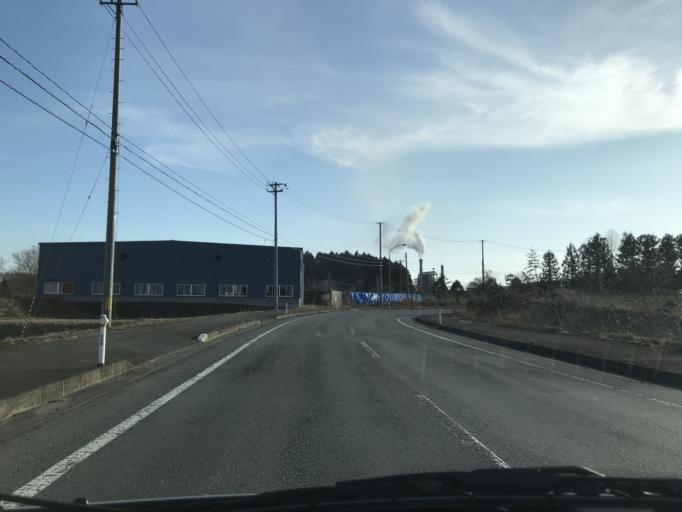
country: JP
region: Iwate
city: Kitakami
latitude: 39.2366
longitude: 141.0969
